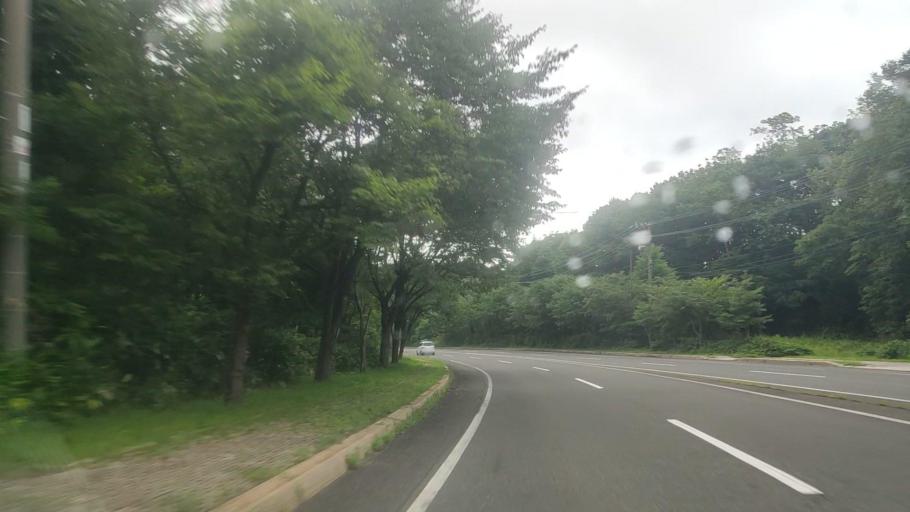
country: JP
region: Hokkaido
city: Shiraoi
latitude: 42.4702
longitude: 141.1496
